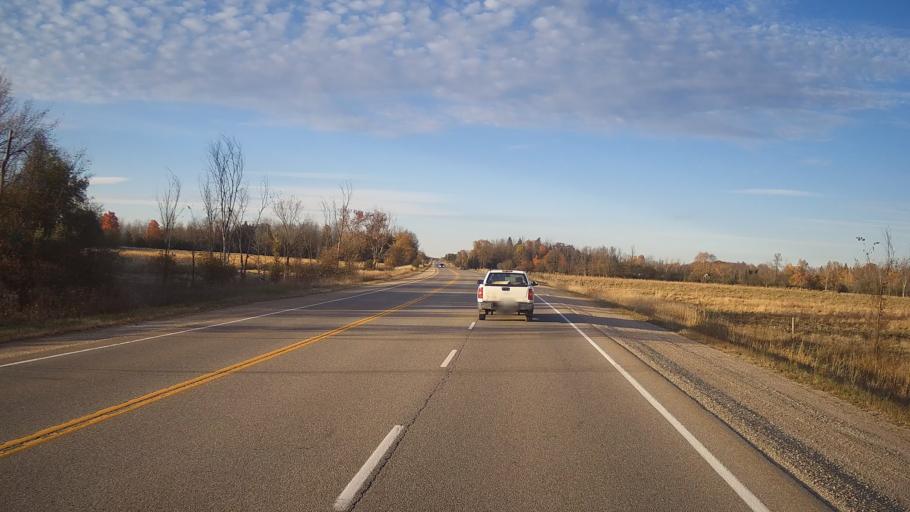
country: CA
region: Ontario
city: Perth
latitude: 44.9791
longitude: -76.2265
